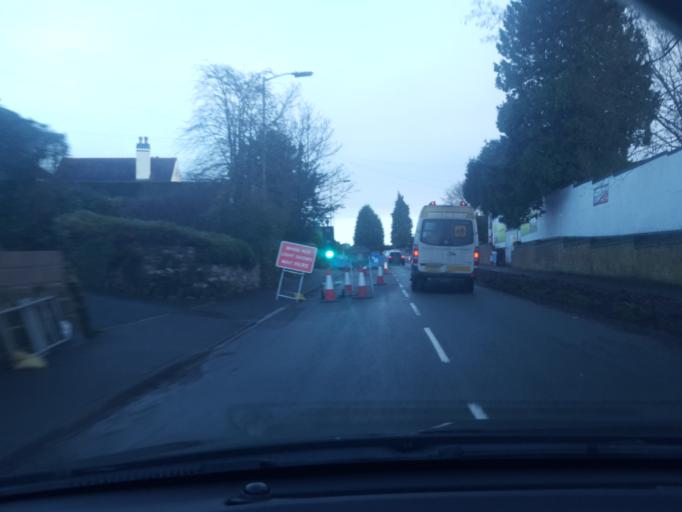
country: GB
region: England
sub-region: Staffordshire
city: Codsall
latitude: 52.6319
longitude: -2.2064
